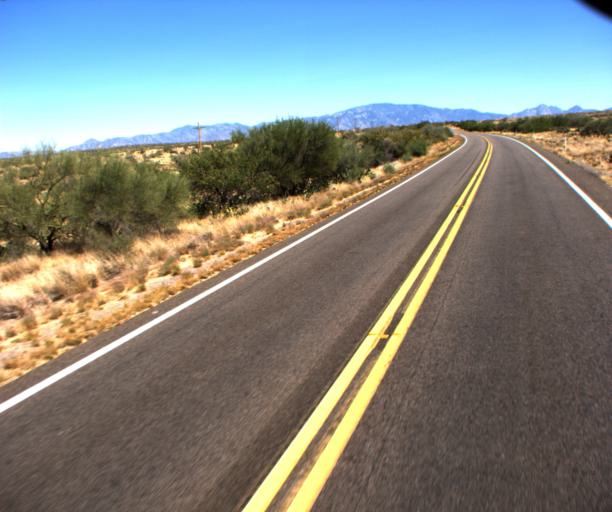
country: US
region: Arizona
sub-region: Pima County
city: Catalina
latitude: 32.6312
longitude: -111.0050
